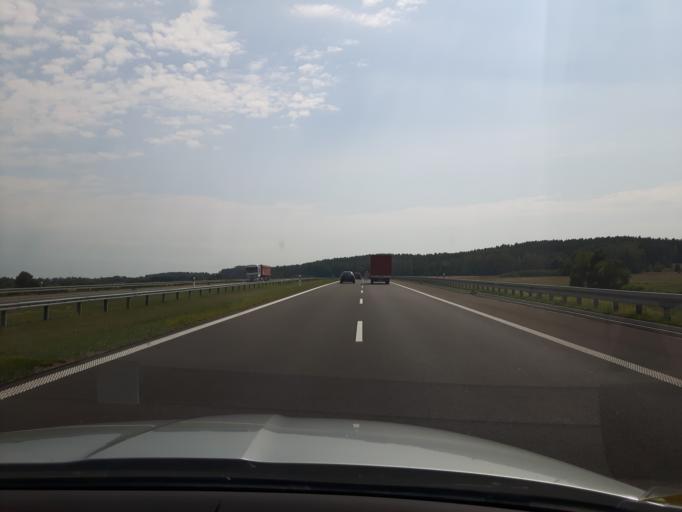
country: PL
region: Warmian-Masurian Voivodeship
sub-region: Powiat nidzicki
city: Nidzica
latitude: 53.3836
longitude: 20.3718
